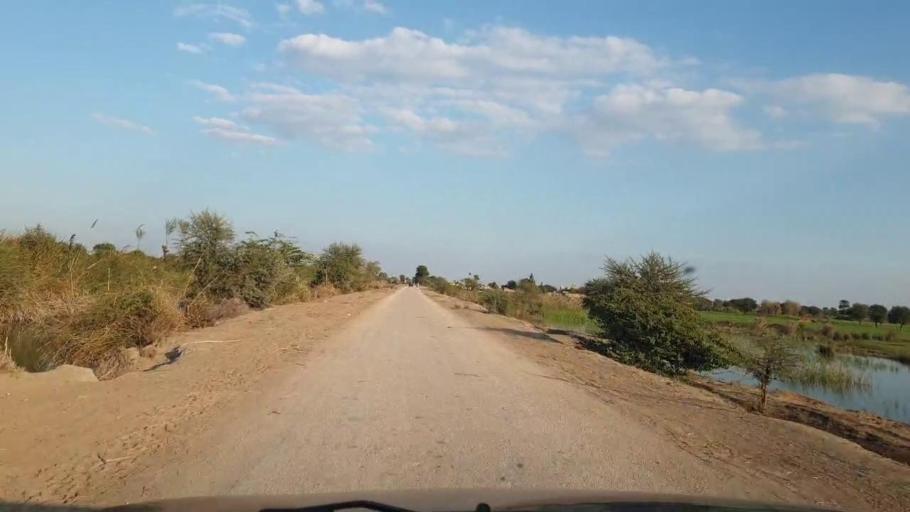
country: PK
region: Sindh
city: Sinjhoro
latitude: 25.9935
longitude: 68.7628
